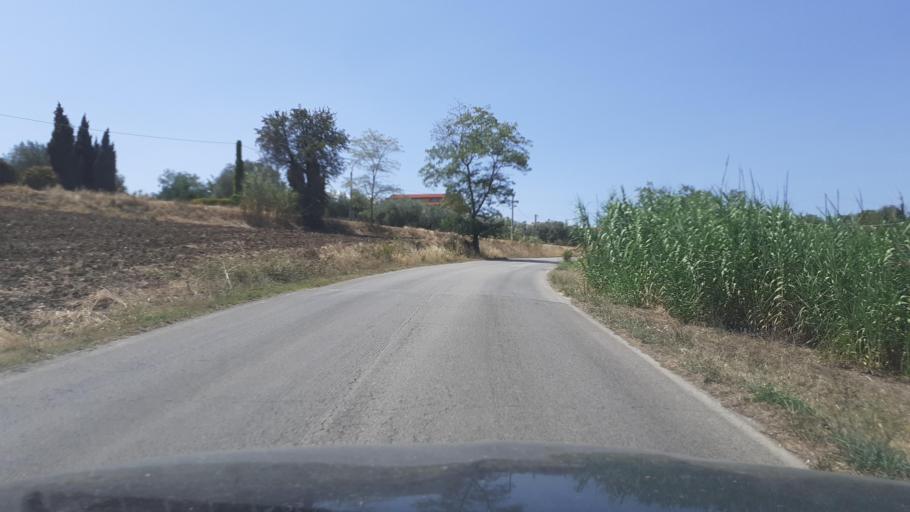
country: IT
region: Abruzzo
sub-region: Provincia di Chieti
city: Santa Maria Imbaro
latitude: 42.2149
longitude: 14.4593
